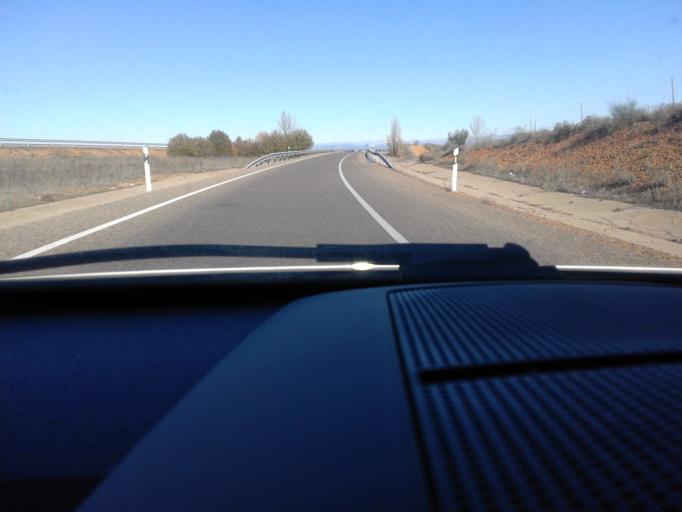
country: ES
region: Castille and Leon
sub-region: Provincia de Leon
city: Onzonilla
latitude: 42.5068
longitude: -5.5969
